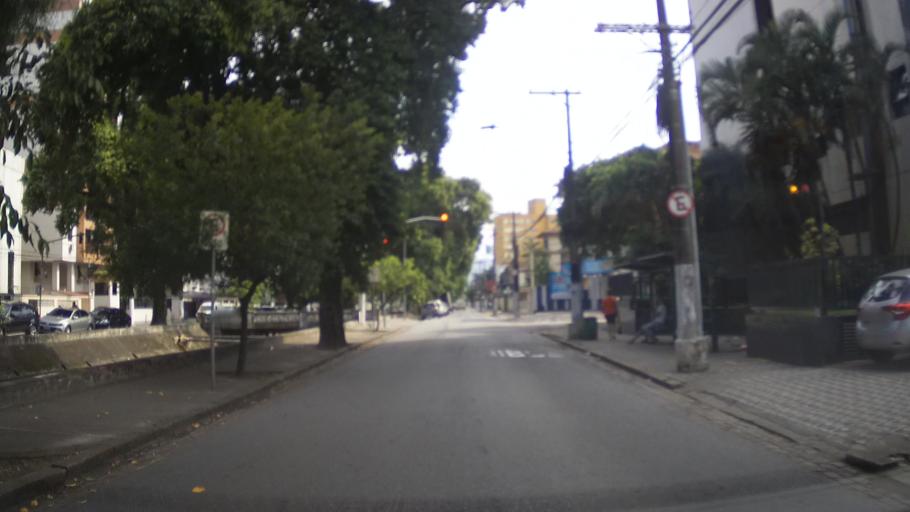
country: BR
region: Sao Paulo
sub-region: Santos
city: Santos
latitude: -23.9560
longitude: -46.3262
